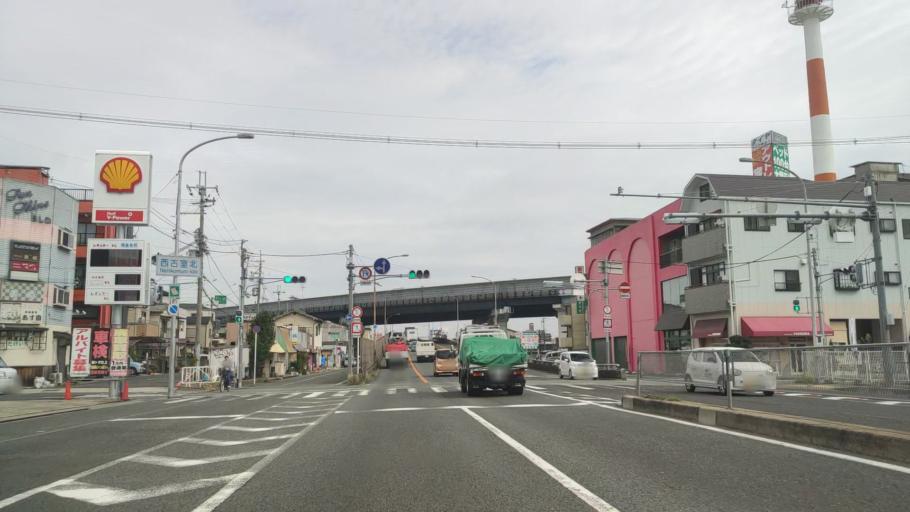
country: JP
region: Osaka
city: Kashihara
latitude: 34.5677
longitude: 135.6055
